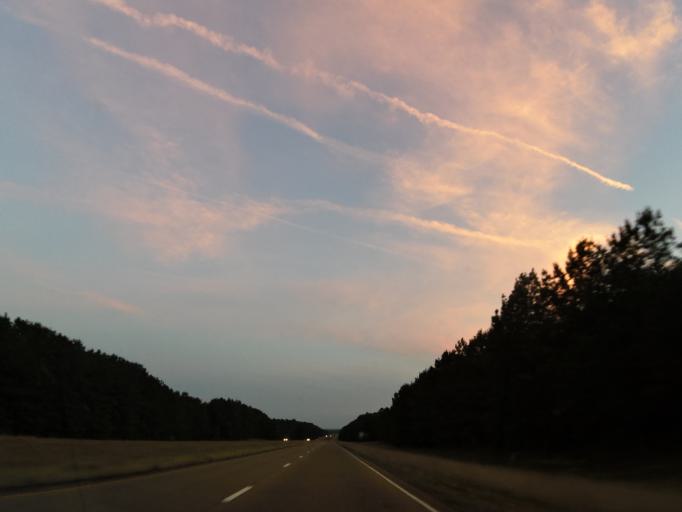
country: US
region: Mississippi
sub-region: Lauderdale County
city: Meridian Station
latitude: 32.5694
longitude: -88.5039
